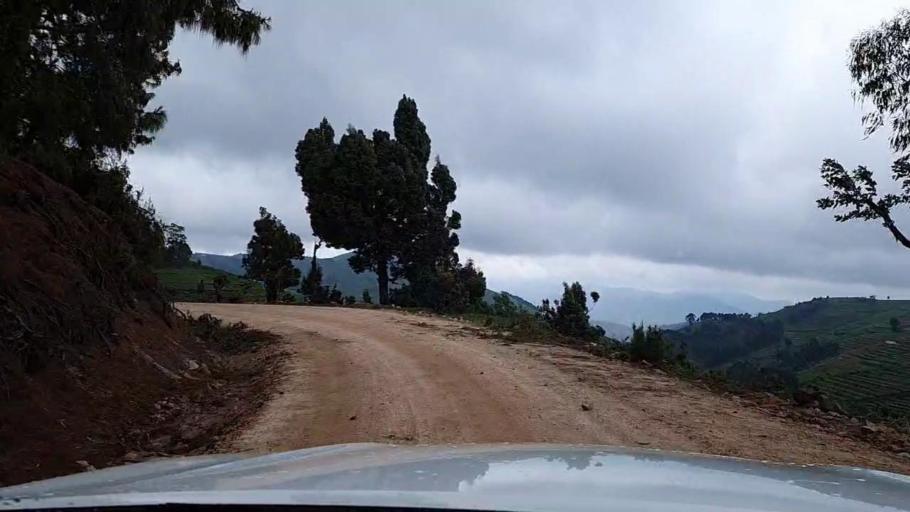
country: RW
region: Western Province
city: Kibuye
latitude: -2.3014
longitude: 29.3833
